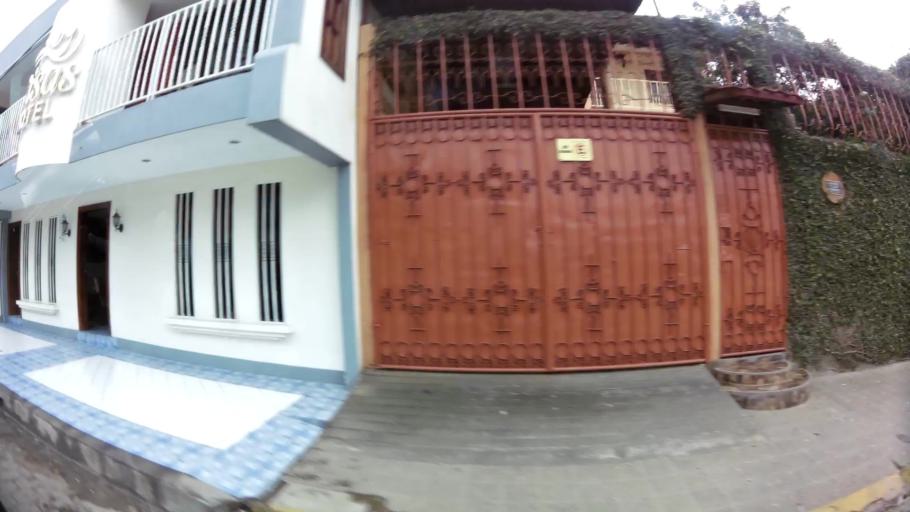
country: NI
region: Matagalpa
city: Matagalpa
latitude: 12.9307
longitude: -85.9161
